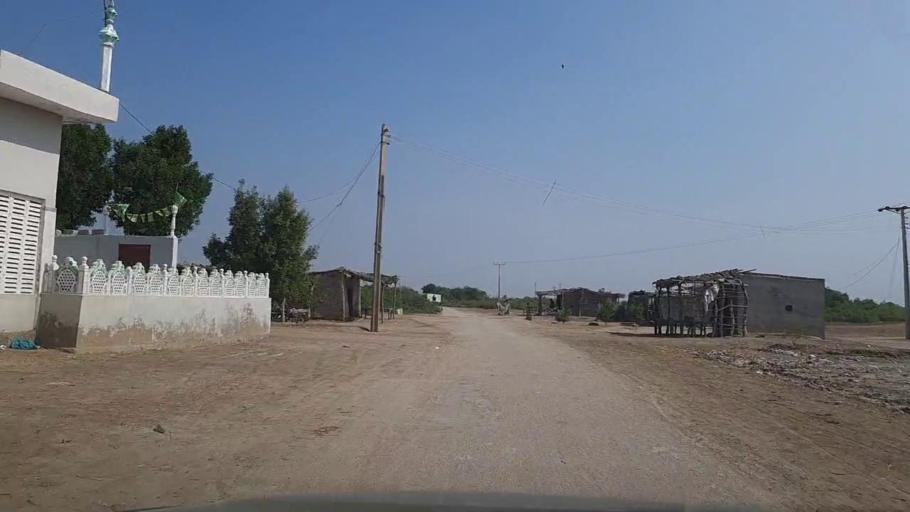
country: PK
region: Sindh
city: Thatta
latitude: 24.5928
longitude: 67.9469
